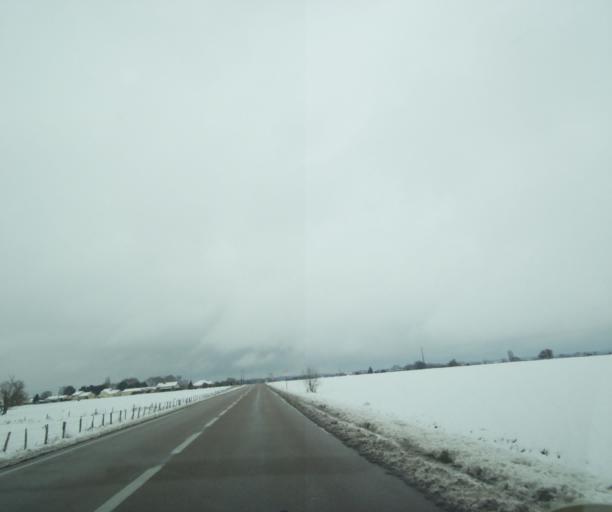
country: FR
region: Champagne-Ardenne
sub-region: Departement de la Haute-Marne
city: Montier-en-Der
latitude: 48.4627
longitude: 4.7585
